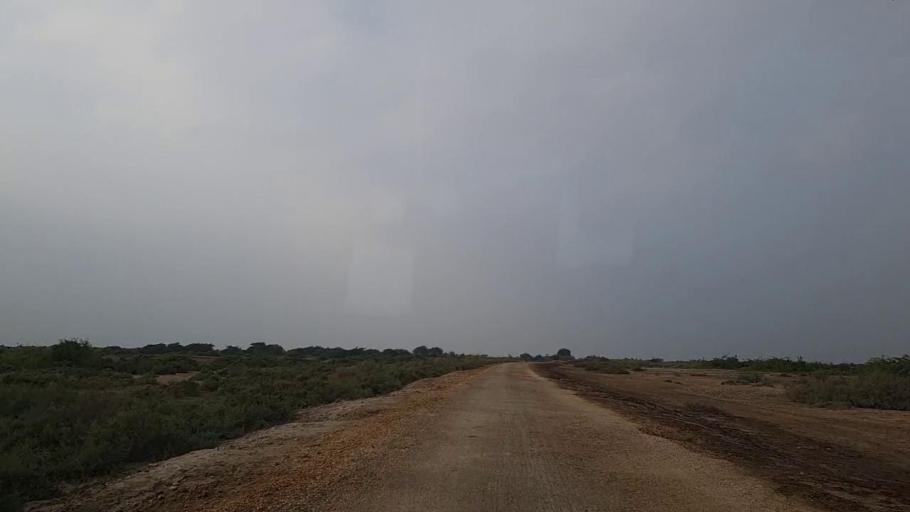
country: PK
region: Sindh
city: Mirpur Sakro
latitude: 24.6052
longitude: 67.5166
